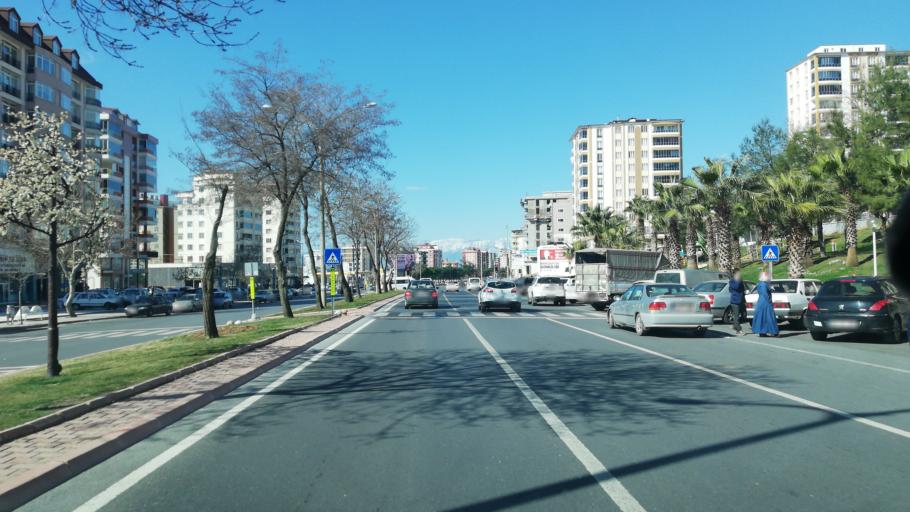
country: TR
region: Kahramanmaras
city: Kahramanmaras
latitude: 37.5930
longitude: 36.8612
